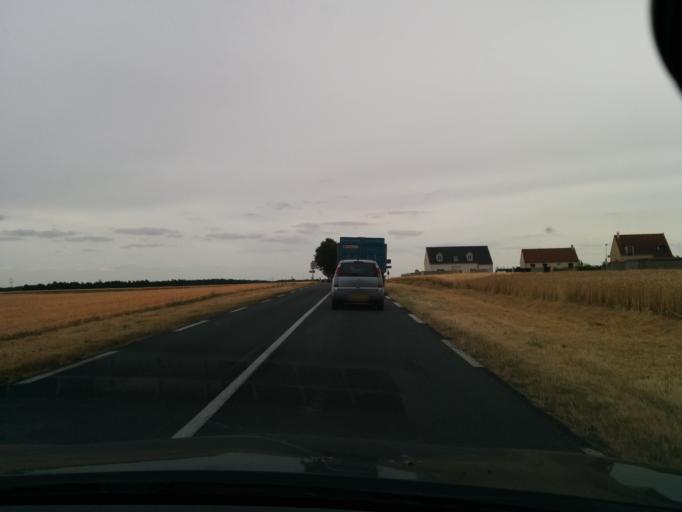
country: FR
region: Ile-de-France
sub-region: Departement de l'Essonne
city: Pussay
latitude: 48.3763
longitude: 1.9783
